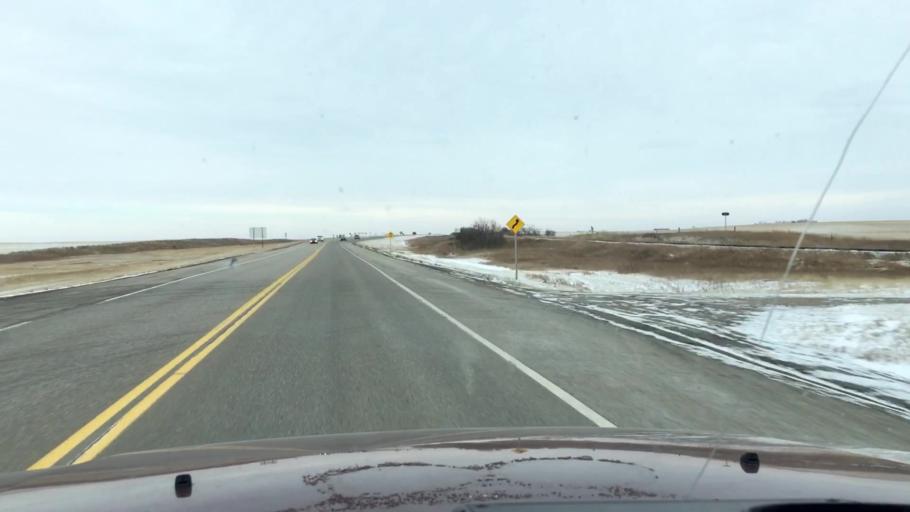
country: CA
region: Saskatchewan
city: Moose Jaw
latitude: 50.8454
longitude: -105.5561
